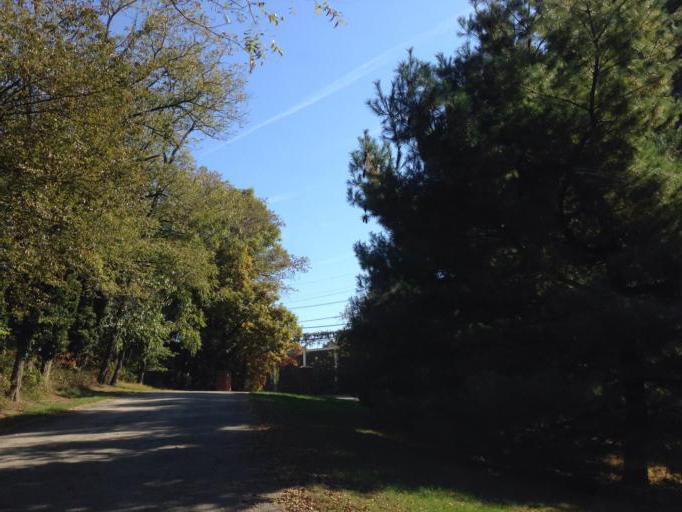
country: US
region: Maryland
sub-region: Howard County
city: Columbia
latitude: 39.2525
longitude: -76.8251
